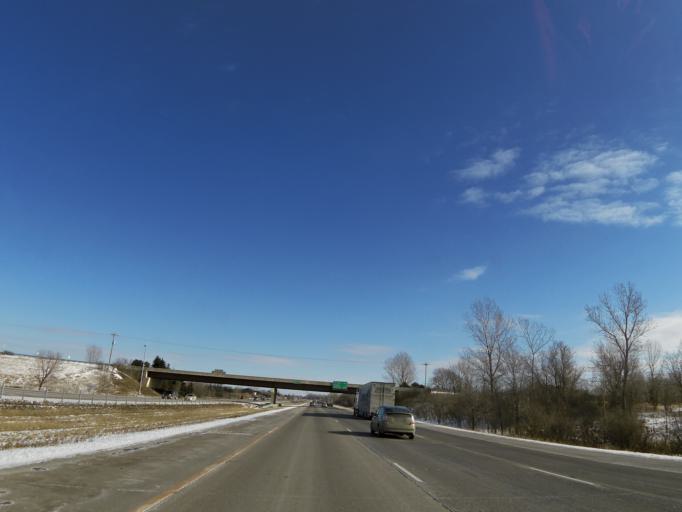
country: US
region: Minnesota
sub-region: Washington County
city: Lake Elmo
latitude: 44.9485
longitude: -92.8451
